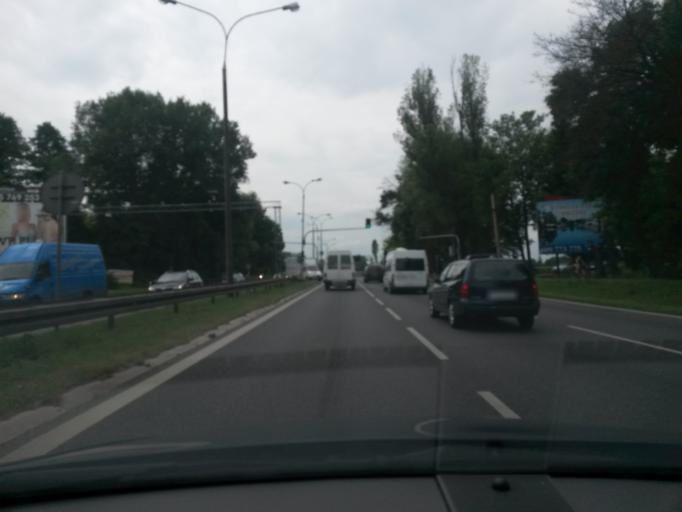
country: PL
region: Masovian Voivodeship
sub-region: Powiat pruszkowski
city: Nowe Grocholice
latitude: 52.1470
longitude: 20.9120
